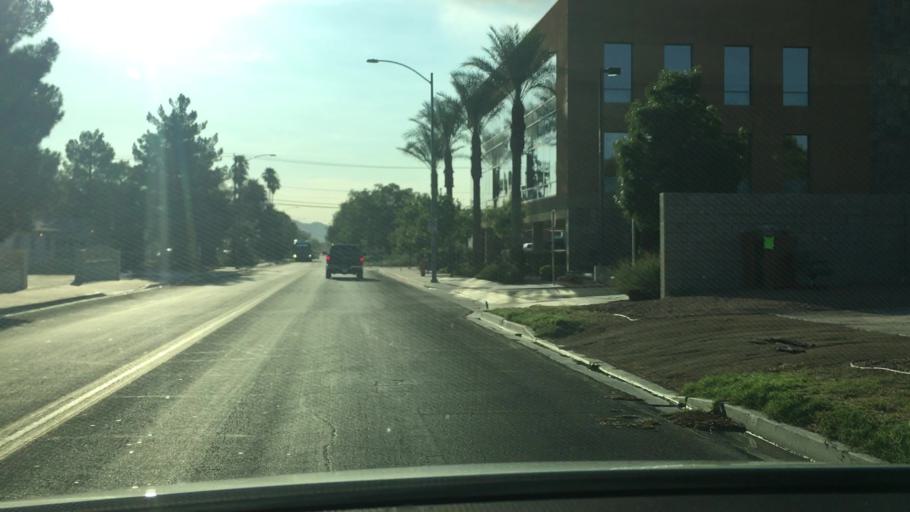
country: US
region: Nevada
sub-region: Clark County
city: Las Vegas
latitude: 36.1643
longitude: -115.1710
